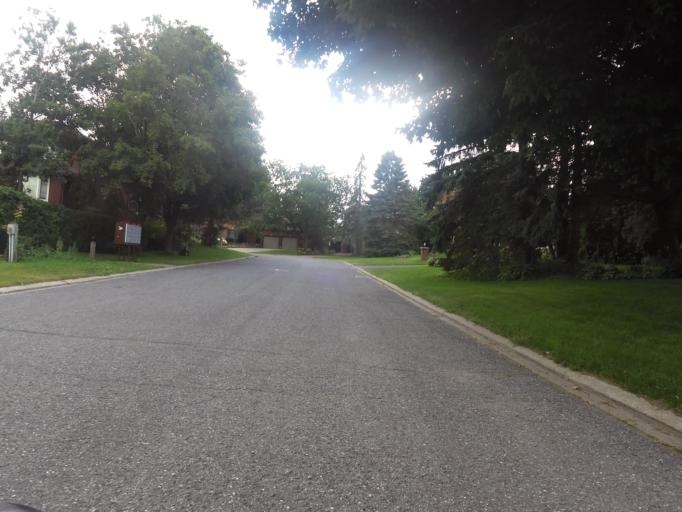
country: CA
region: Ontario
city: Bells Corners
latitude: 45.3246
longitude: -75.9108
